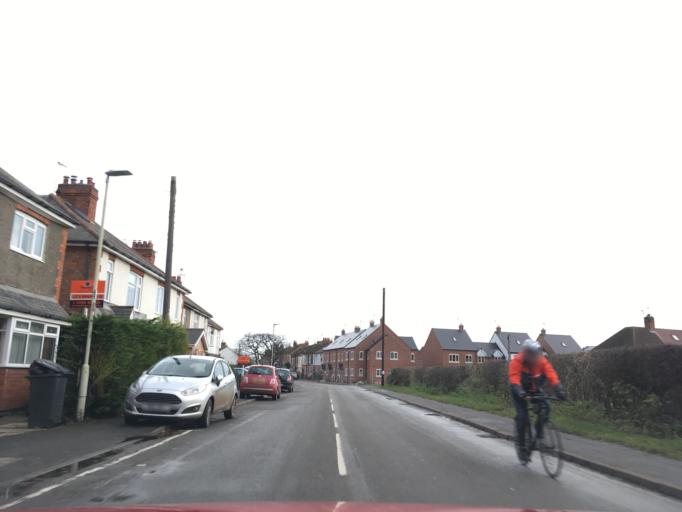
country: GB
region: England
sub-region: Leicestershire
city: Kegworth
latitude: 52.8400
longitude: -1.2764
